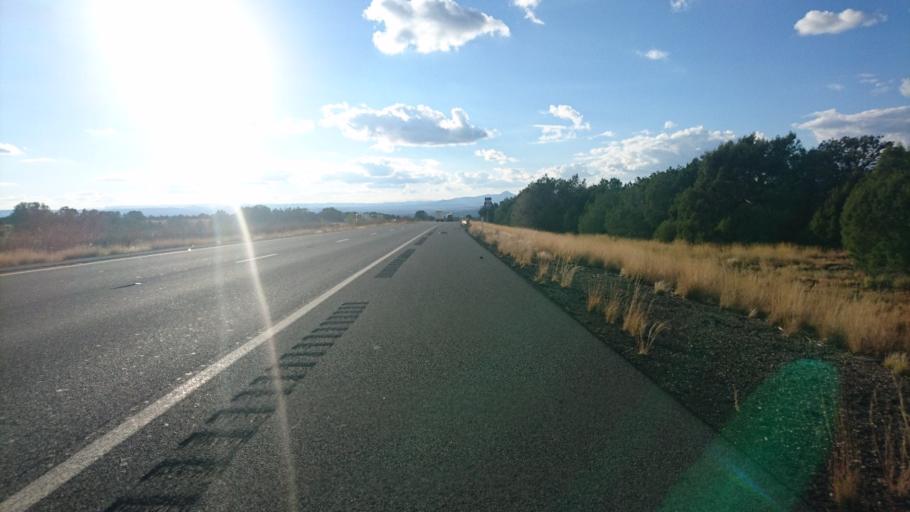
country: US
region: Arizona
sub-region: Coconino County
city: Williams
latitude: 35.2163
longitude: -112.3812
